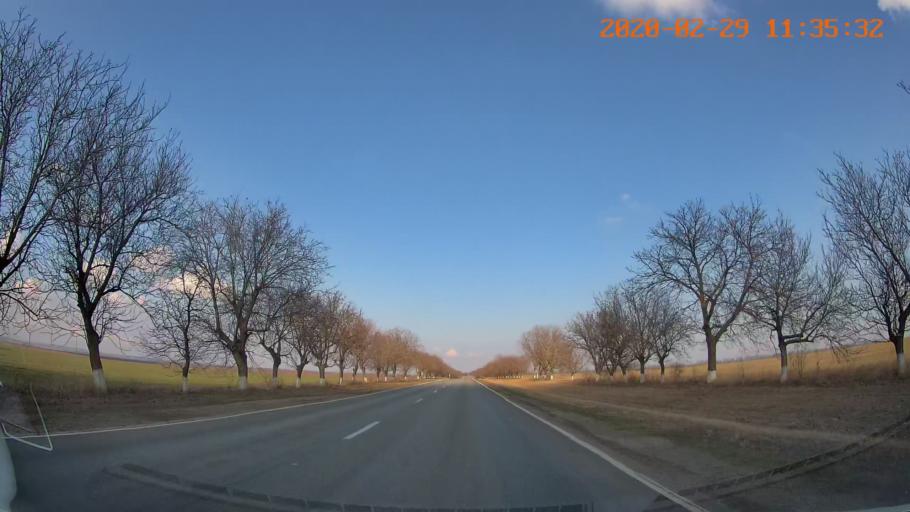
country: MD
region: Rezina
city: Saharna
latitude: 47.5821
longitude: 29.0627
